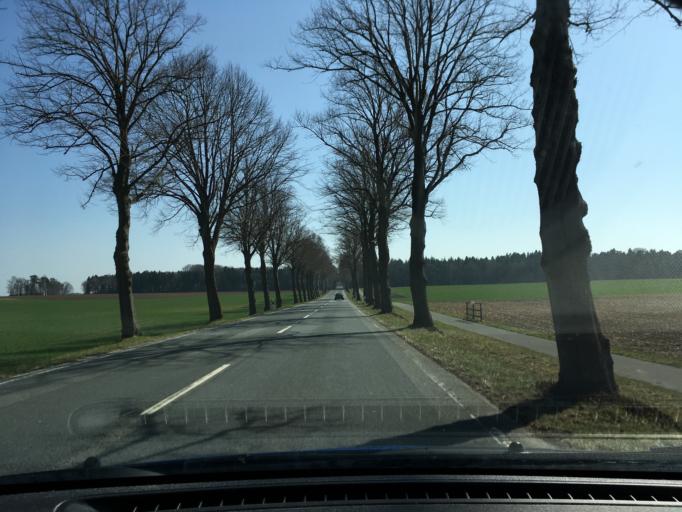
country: DE
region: Lower Saxony
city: Wriedel
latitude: 53.0662
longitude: 10.2856
